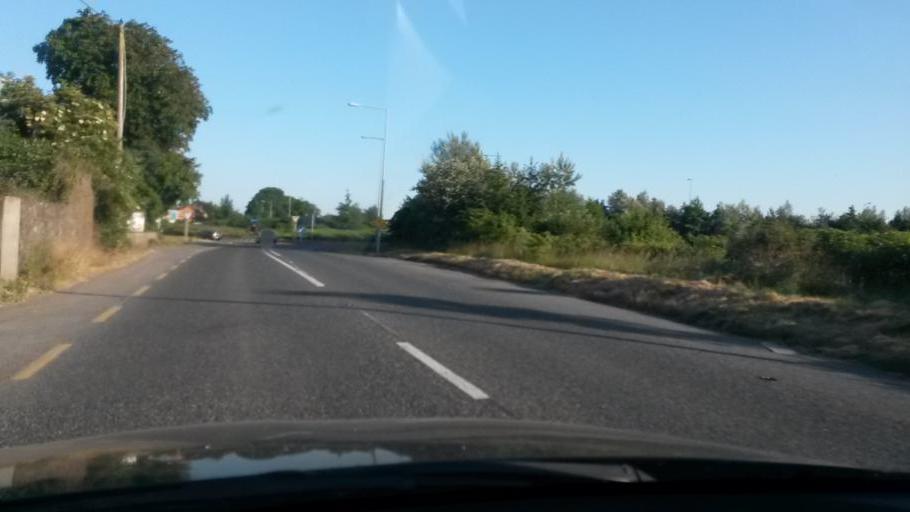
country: IE
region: Leinster
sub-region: Dublin City
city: Finglas
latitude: 53.4357
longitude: -6.3346
